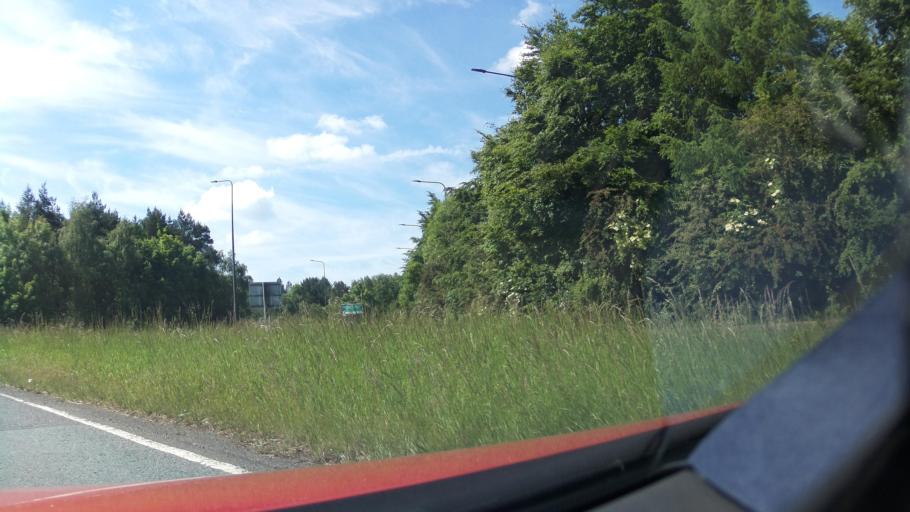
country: GB
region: England
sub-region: North Lincolnshire
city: Scawby
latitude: 53.5458
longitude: -0.5577
